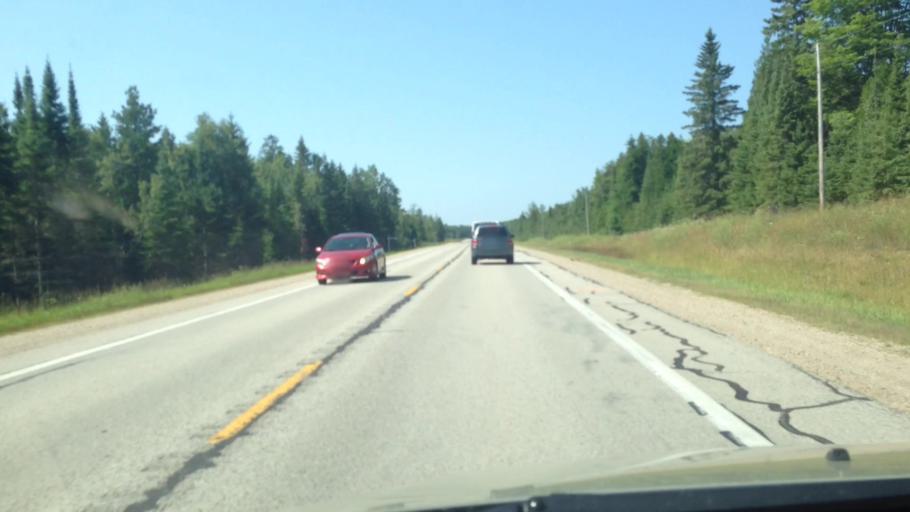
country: US
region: Michigan
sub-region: Delta County
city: Escanaba
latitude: 45.5694
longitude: -87.2542
